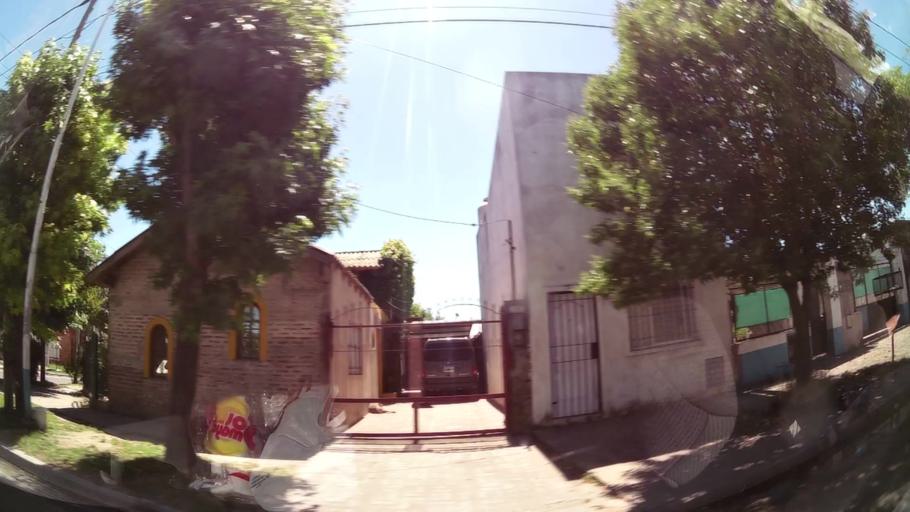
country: AR
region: Buenos Aires
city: Hurlingham
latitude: -34.4893
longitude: -58.6656
